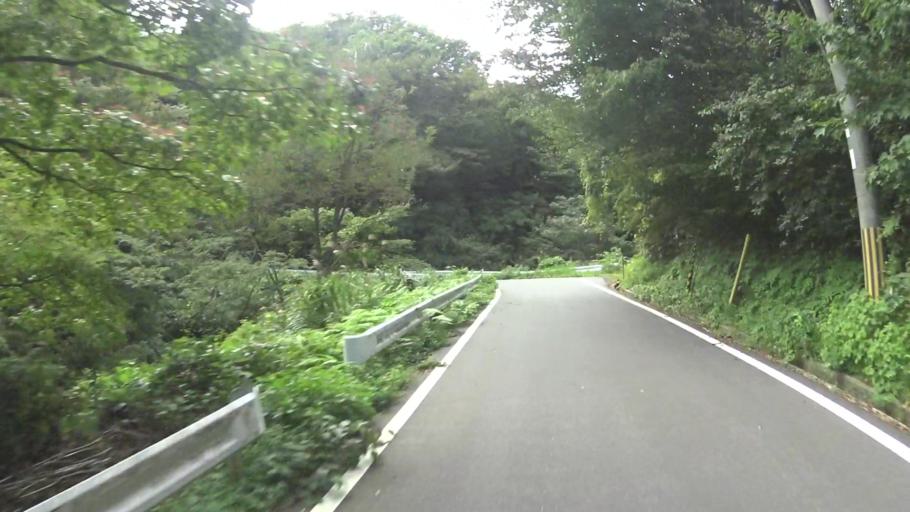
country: JP
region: Kyoto
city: Miyazu
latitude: 35.7292
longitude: 135.2032
